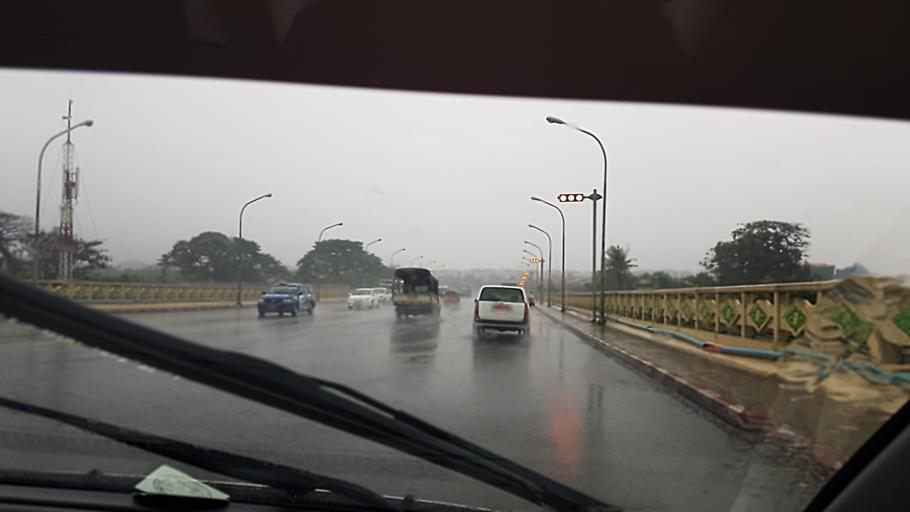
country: MM
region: Yangon
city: Yangon
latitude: 16.7787
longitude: 96.1841
